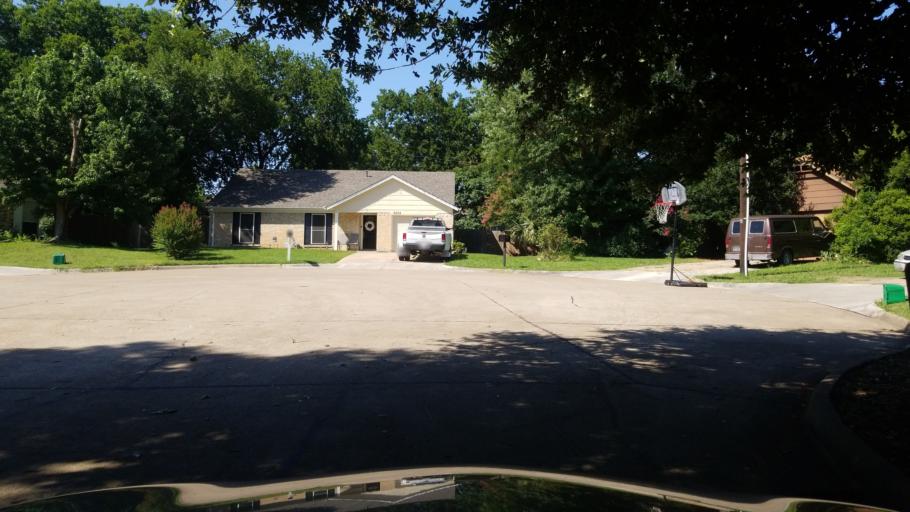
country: US
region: Texas
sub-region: Dallas County
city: Grand Prairie
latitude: 32.6798
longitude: -97.0162
